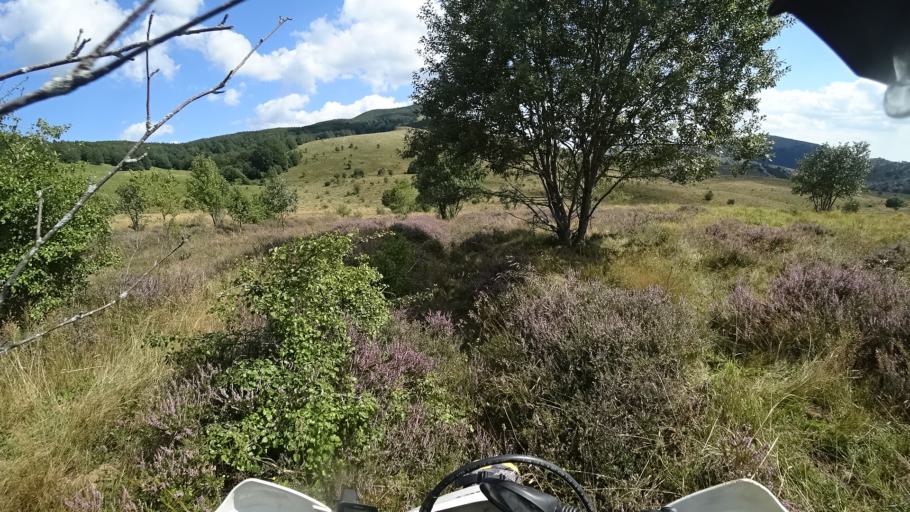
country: HR
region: Zadarska
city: Gracac
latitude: 44.4174
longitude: 16.0004
